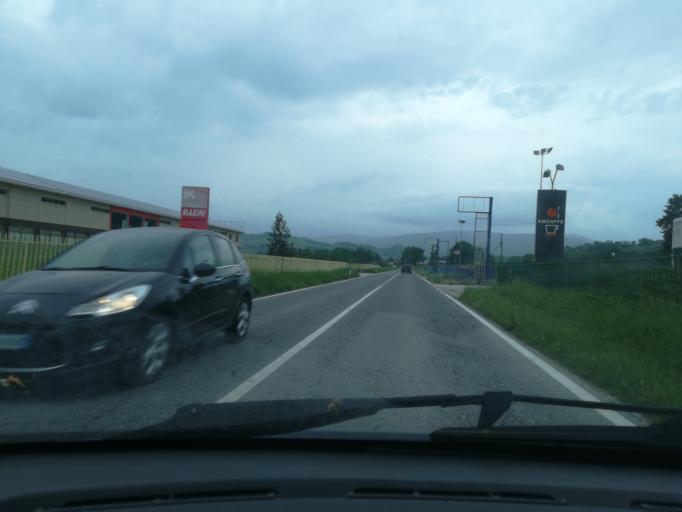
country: IT
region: The Marches
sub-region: Provincia di Macerata
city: San Severino Marche
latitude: 43.2569
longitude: 13.2341
